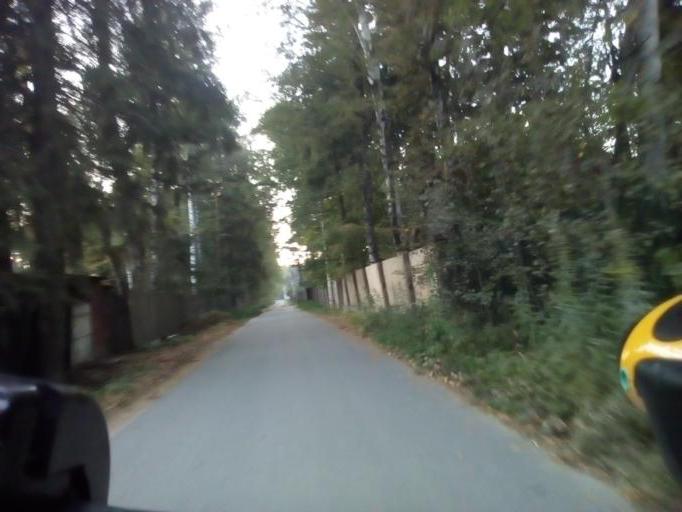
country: RU
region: Moskovskaya
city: Kratovo
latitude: 55.5938
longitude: 38.1977
